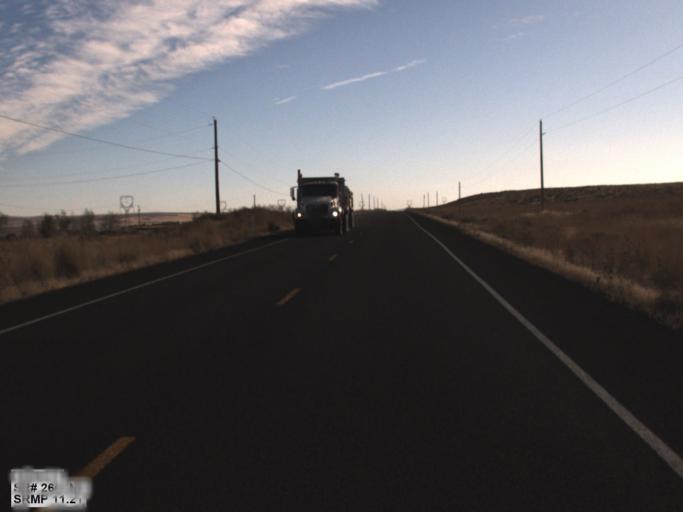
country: US
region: Washington
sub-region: Franklin County
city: Connell
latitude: 46.6347
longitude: -118.7833
